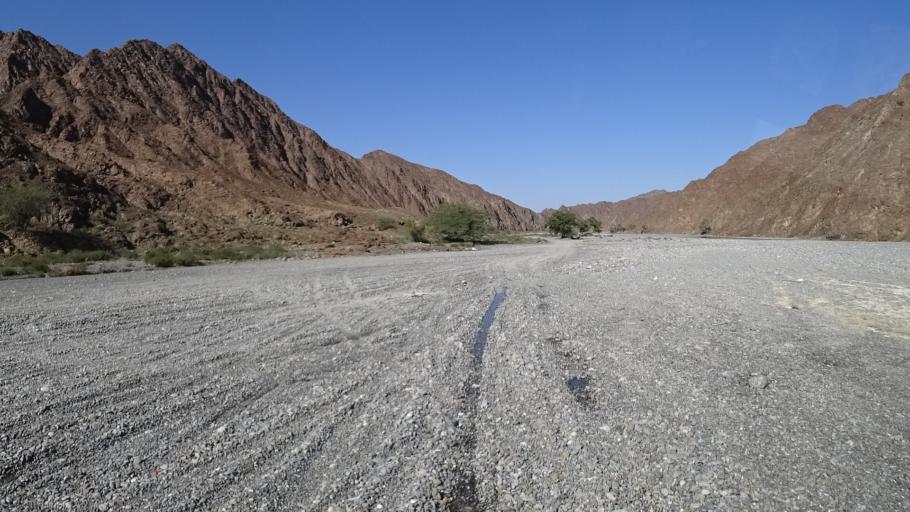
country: OM
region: Al Batinah
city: Bayt al `Awabi
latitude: 23.4014
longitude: 57.6657
